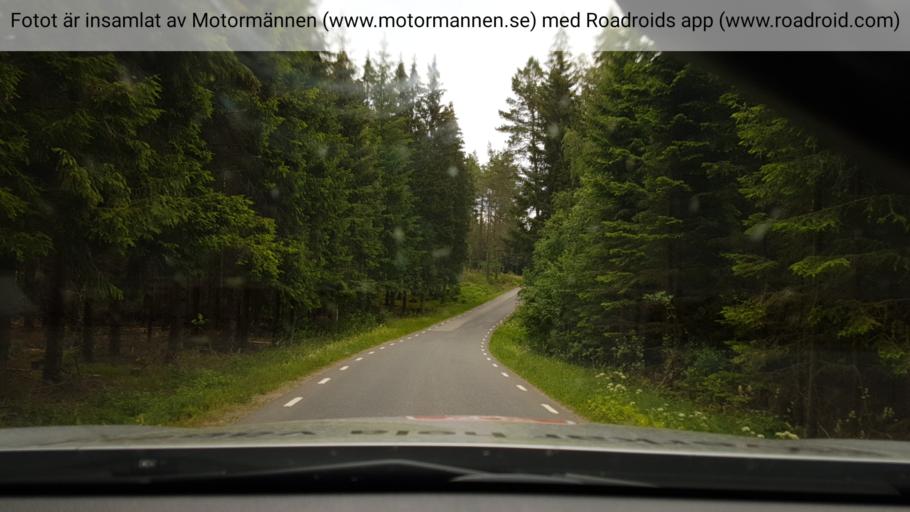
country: SE
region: Joenkoeping
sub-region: Mullsjo Kommun
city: Mullsjoe
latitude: 57.9549
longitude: 13.7027
